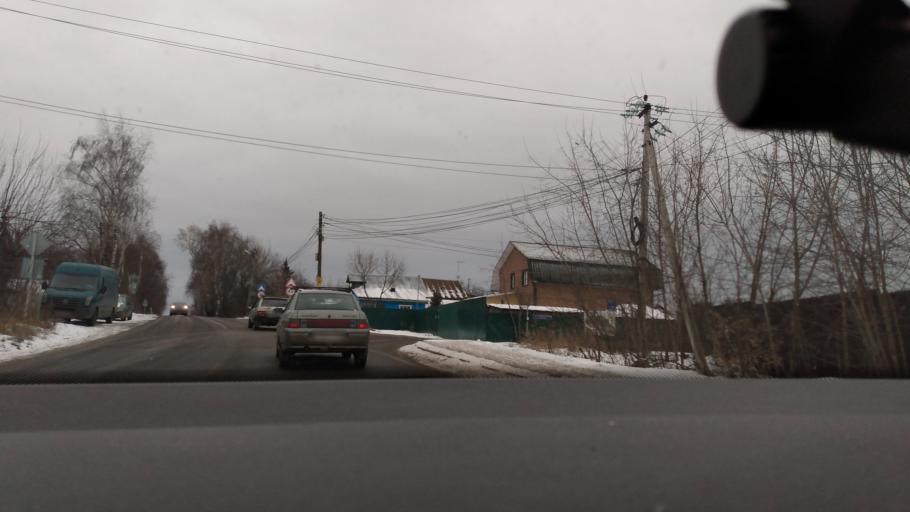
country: RU
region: Moskovskaya
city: Chornaya
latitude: 55.7075
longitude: 38.0479
